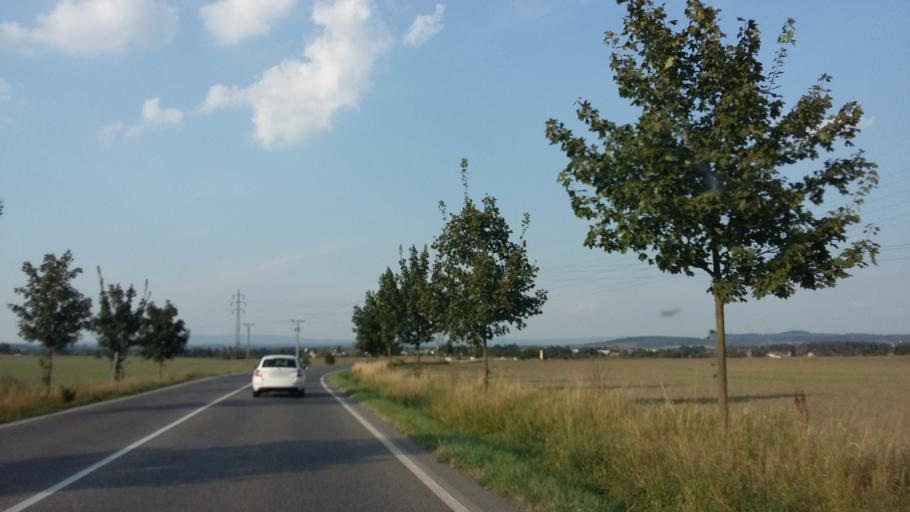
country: CZ
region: Central Bohemia
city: Bakov nad Jizerou
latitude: 50.4616
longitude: 14.9323
